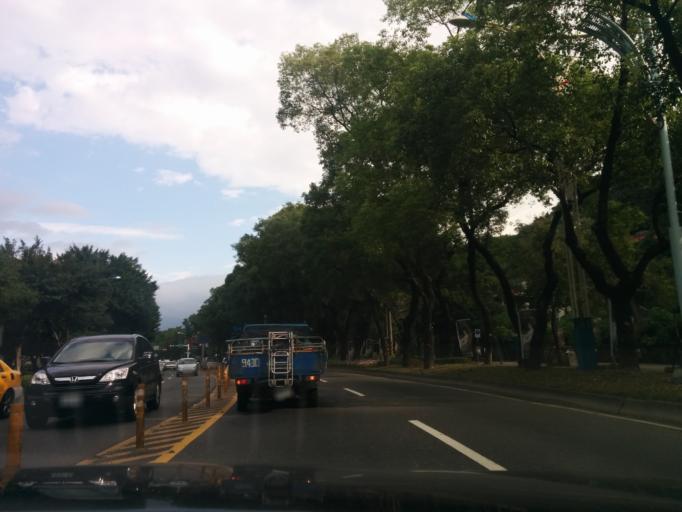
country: TW
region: Taipei
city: Taipei
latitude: 25.0824
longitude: 121.5253
